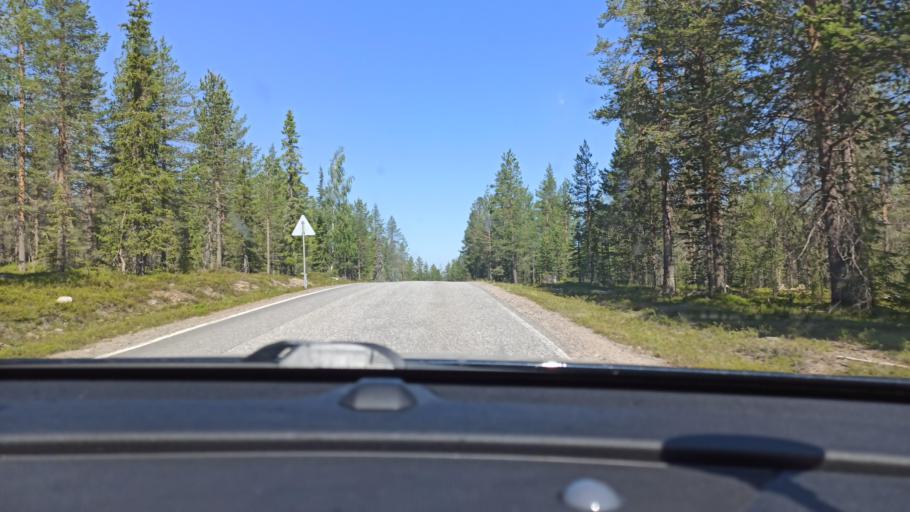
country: FI
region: Lapland
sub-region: Tunturi-Lappi
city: Kolari
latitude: 67.6801
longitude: 24.1389
